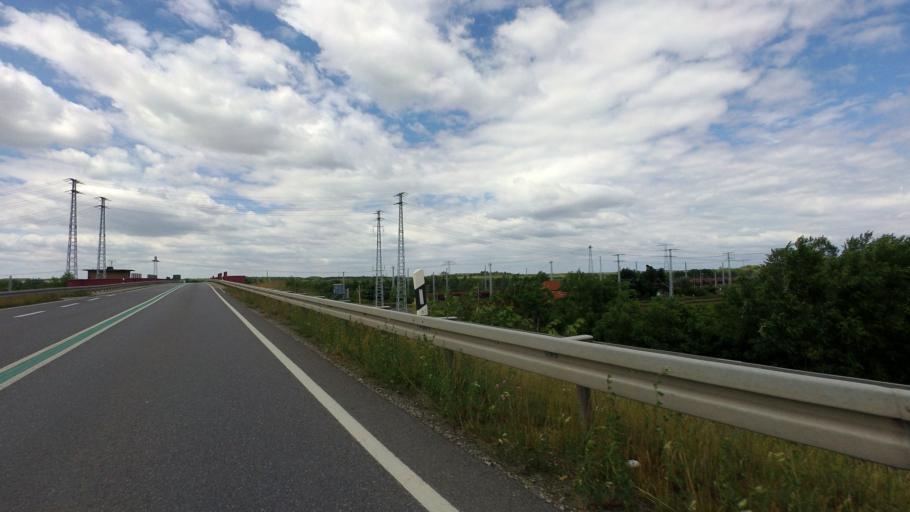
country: DE
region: Brandenburg
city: Senftenberg
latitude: 51.5313
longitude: 14.0155
